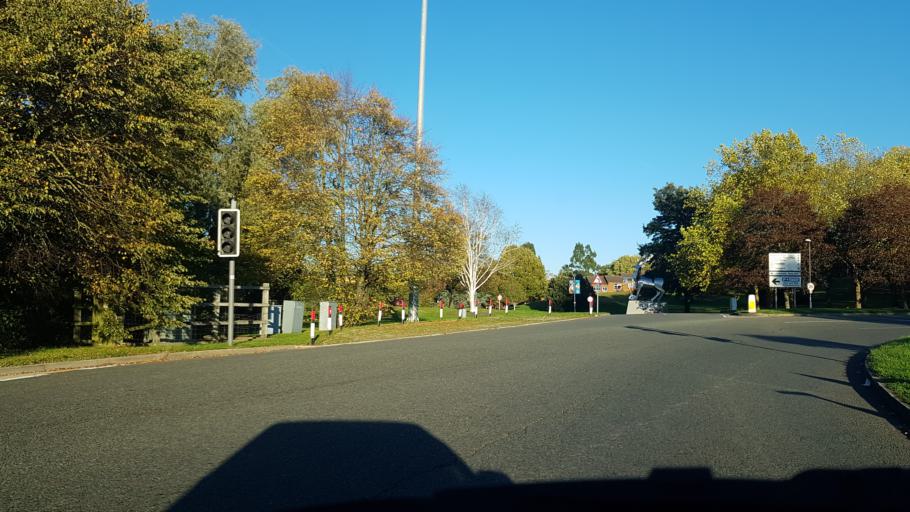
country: GB
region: England
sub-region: Surrey
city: Guildford
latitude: 51.2419
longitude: -0.5964
